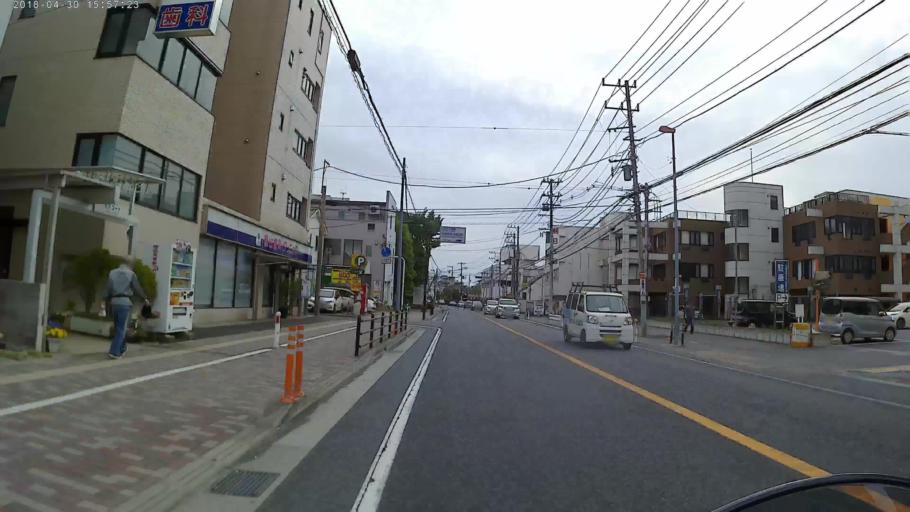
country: JP
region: Tokyo
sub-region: Machida-shi
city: Machida
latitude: 35.5299
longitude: 139.4306
